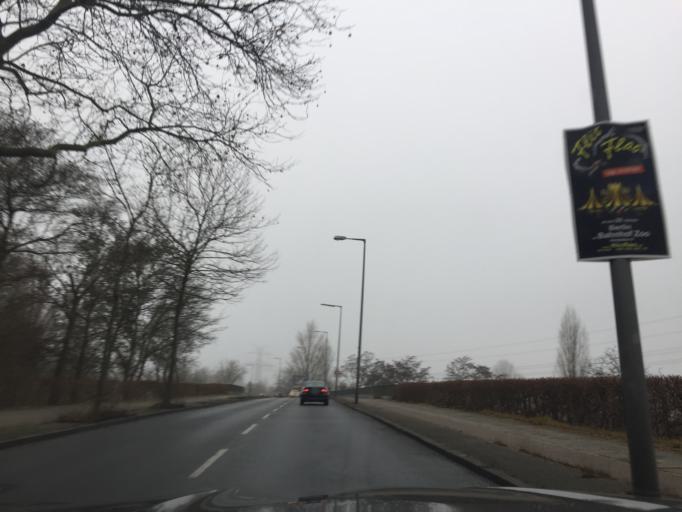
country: DE
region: Berlin
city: Westend
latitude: 52.5276
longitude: 13.2754
